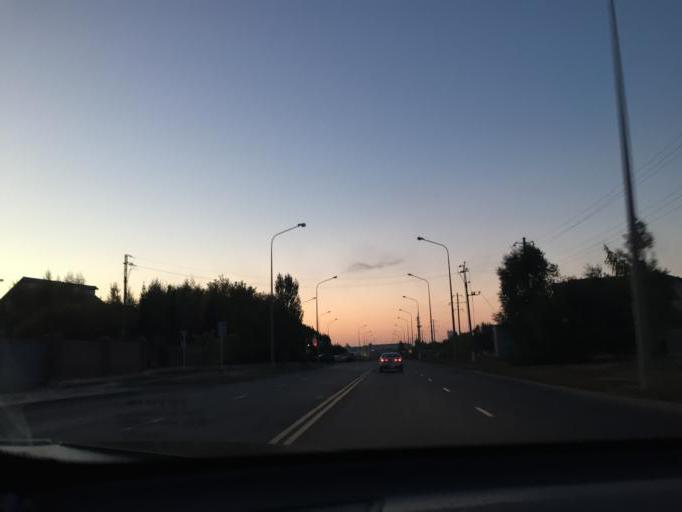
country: KZ
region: Astana Qalasy
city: Astana
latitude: 51.1442
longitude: 71.4525
